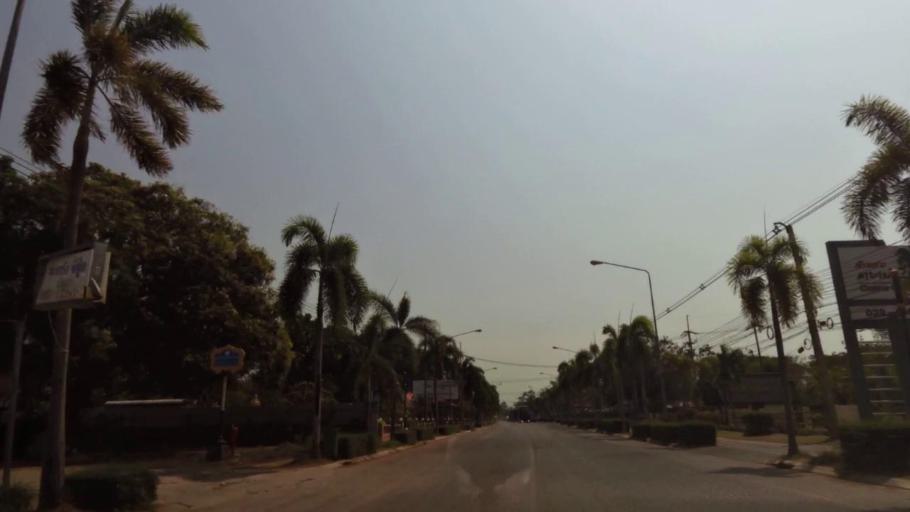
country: TH
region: Chanthaburi
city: Tha Mai
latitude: 12.5532
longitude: 101.9222
